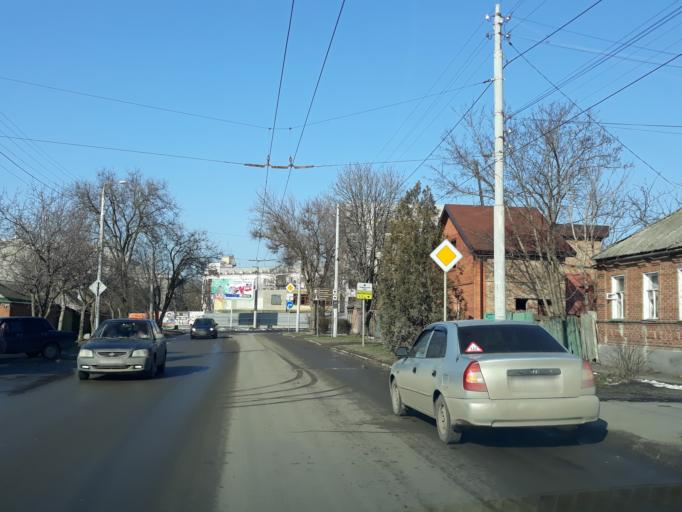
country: RU
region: Rostov
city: Taganrog
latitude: 47.2044
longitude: 38.8975
